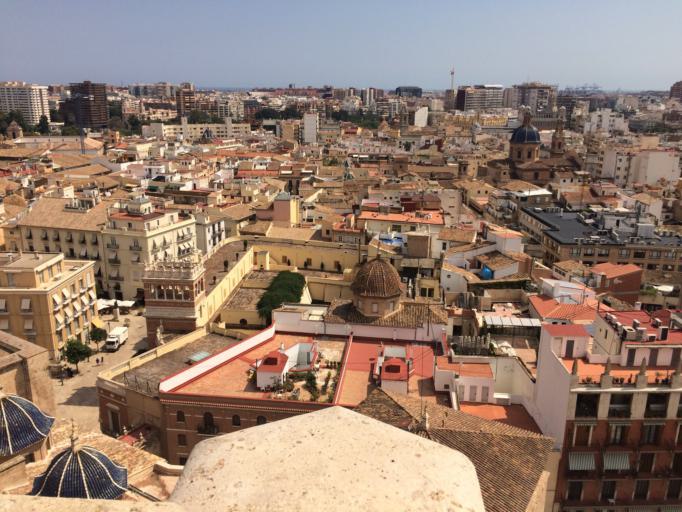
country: ES
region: Valencia
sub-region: Provincia de Valencia
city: Valencia
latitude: 39.4753
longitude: -0.3757
